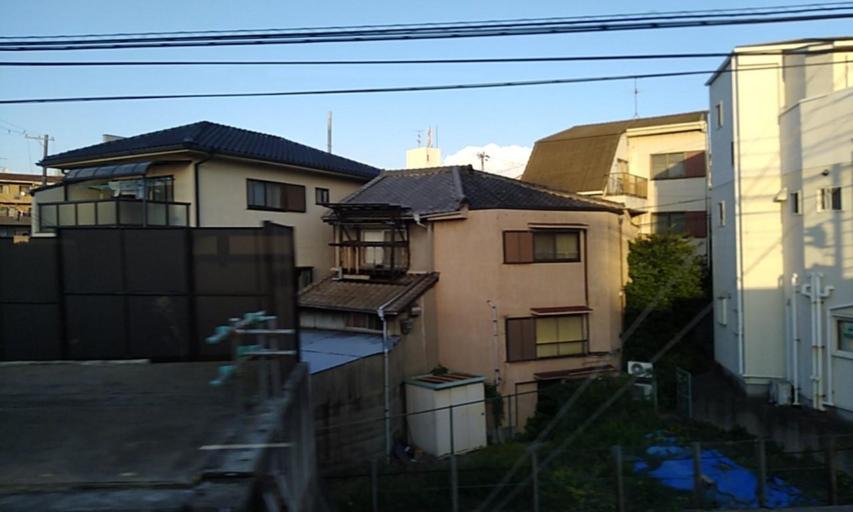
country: JP
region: Osaka
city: Sakai
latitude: 34.6272
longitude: 135.4971
